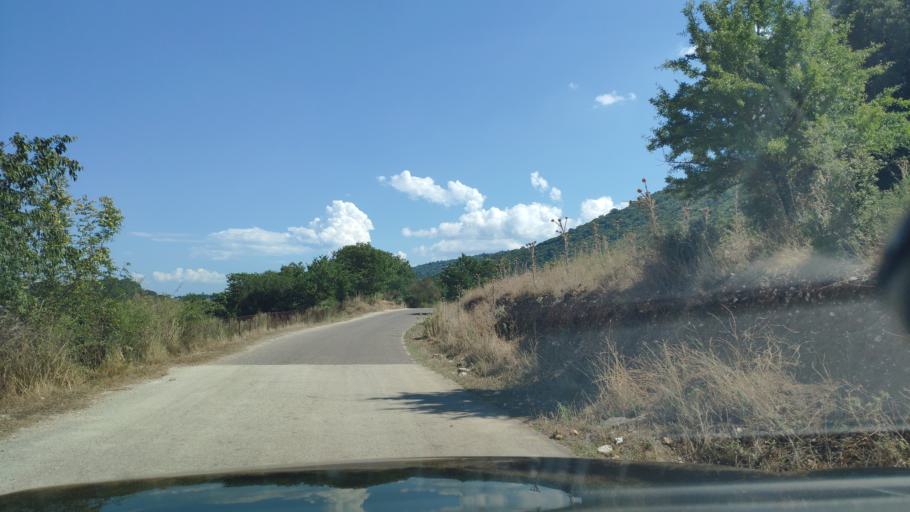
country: GR
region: West Greece
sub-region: Nomos Aitolias kai Akarnanias
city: Katouna
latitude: 38.8325
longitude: 21.0992
